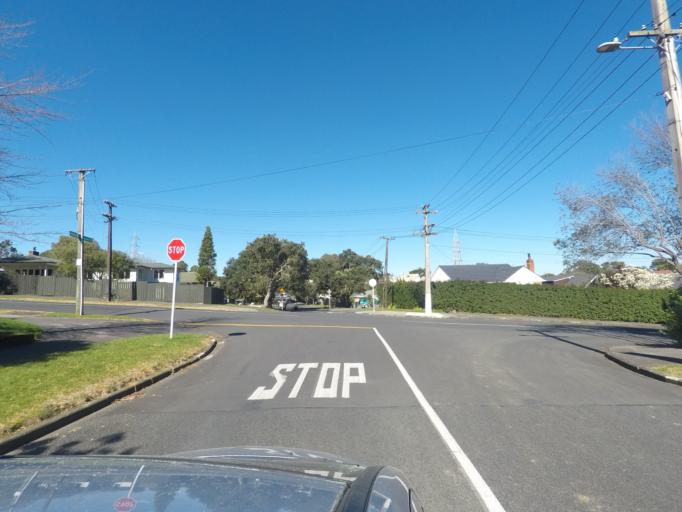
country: NZ
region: Auckland
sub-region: Auckland
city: Waitakere
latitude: -36.9286
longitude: 174.6953
